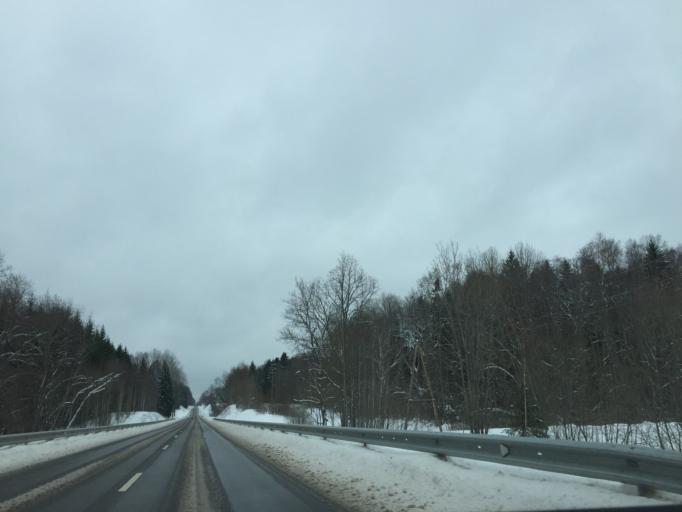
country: LV
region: Ligatne
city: Ligatne
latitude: 57.1351
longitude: 25.0842
